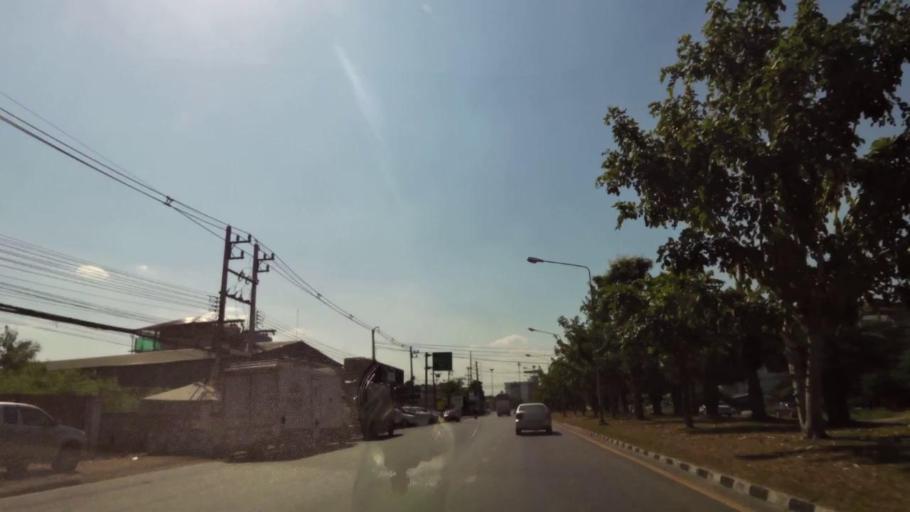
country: TH
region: Nakhon Sawan
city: Nakhon Sawan
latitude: 15.7077
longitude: 100.1133
